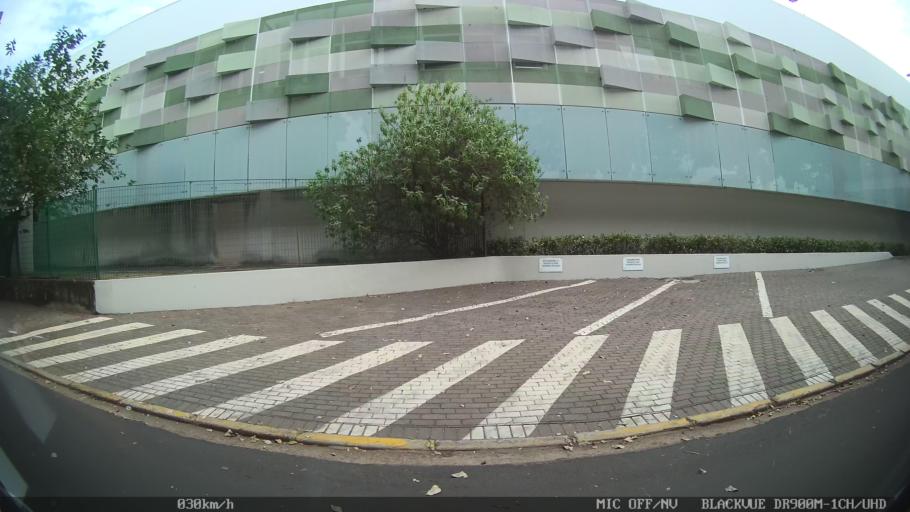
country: BR
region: Sao Paulo
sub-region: Paulinia
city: Paulinia
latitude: -22.7695
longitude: -47.1496
